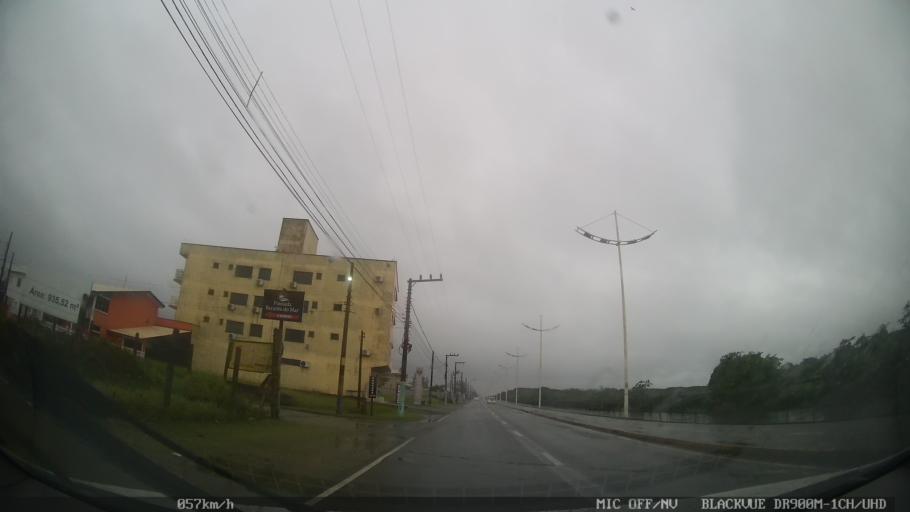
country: BR
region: Santa Catarina
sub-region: Navegantes
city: Navegantes
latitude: -26.8869
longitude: -48.6421
